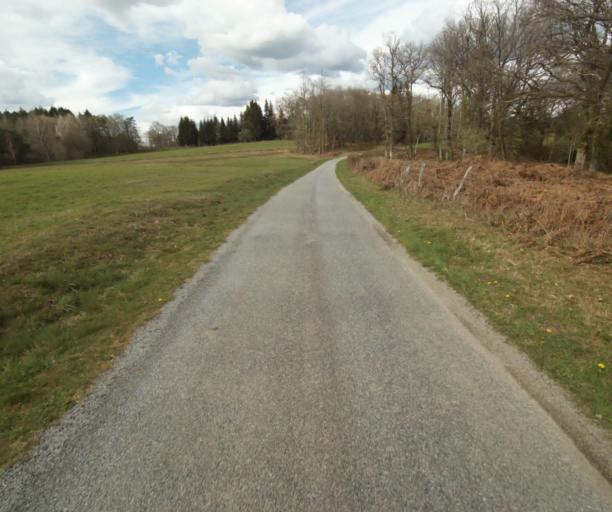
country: FR
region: Limousin
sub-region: Departement de la Correze
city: Argentat
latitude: 45.1960
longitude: 1.9271
